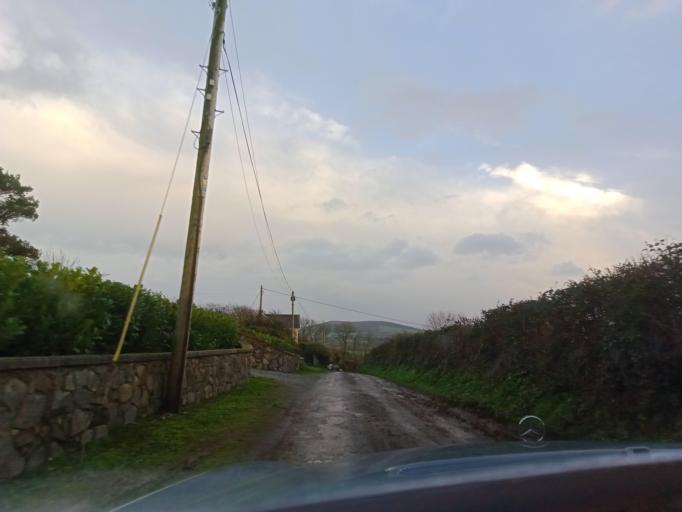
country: IE
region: Leinster
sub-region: Loch Garman
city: New Ross
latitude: 52.3470
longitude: -7.0077
